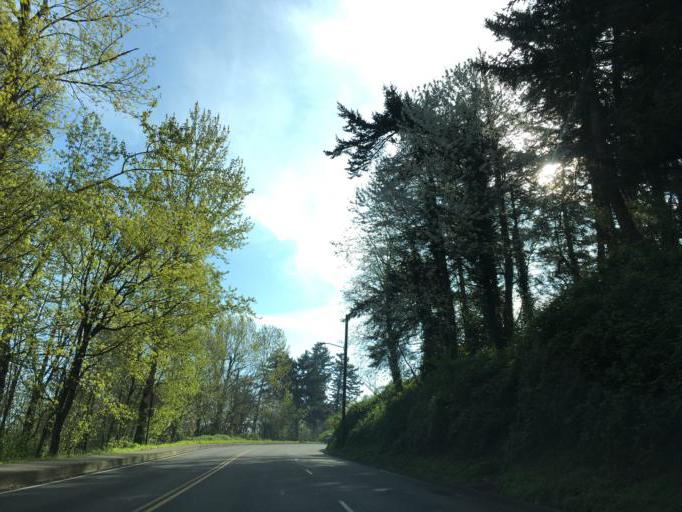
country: US
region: Oregon
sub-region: Multnomah County
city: Wood Village
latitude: 45.5313
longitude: -122.4165
